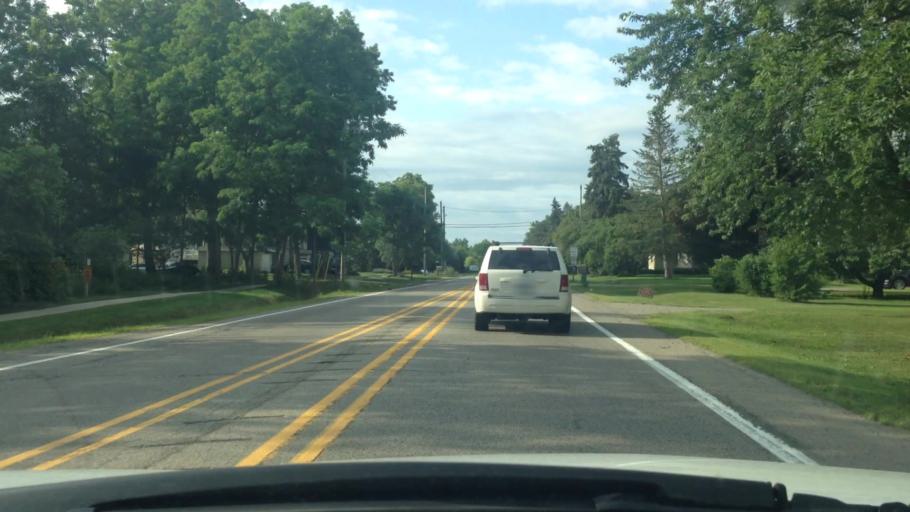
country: US
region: Michigan
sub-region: Oakland County
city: Waterford
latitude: 42.7188
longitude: -83.3493
